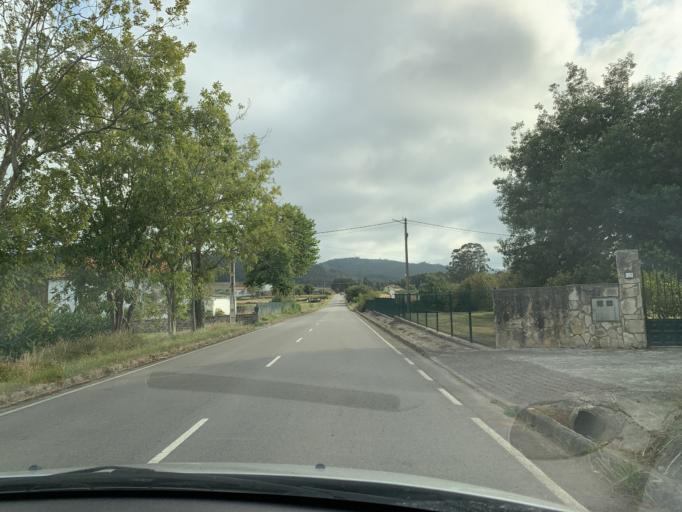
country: ES
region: Asturias
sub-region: Province of Asturias
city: Villaviciosa
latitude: 43.5263
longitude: -5.4345
